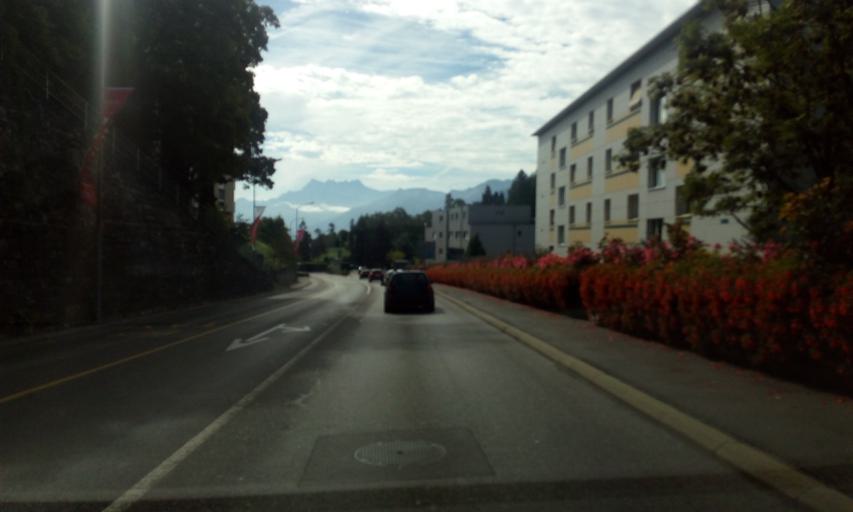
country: CH
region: Vaud
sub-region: Riviera-Pays-d'Enhaut District
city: Le Chatelard
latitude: 46.4516
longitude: 6.8906
